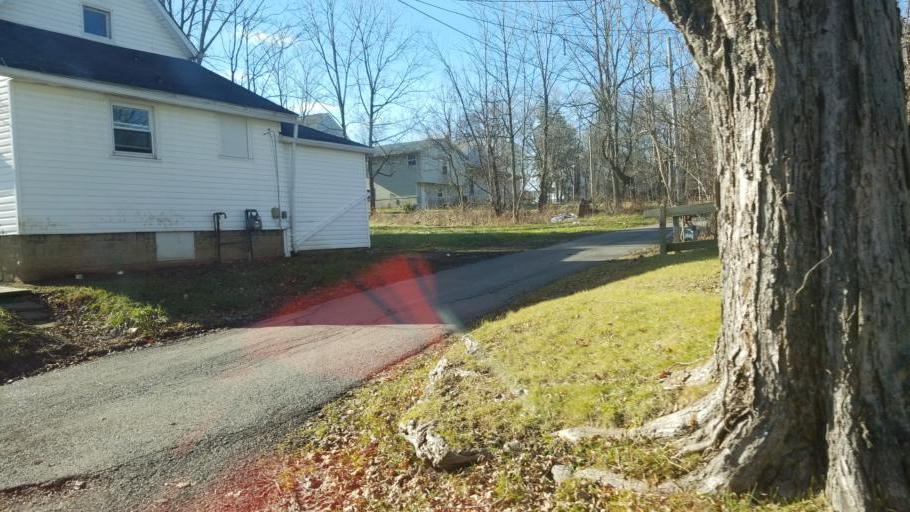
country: US
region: Ohio
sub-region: Richland County
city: Mansfield
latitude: 40.7763
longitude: -82.5242
